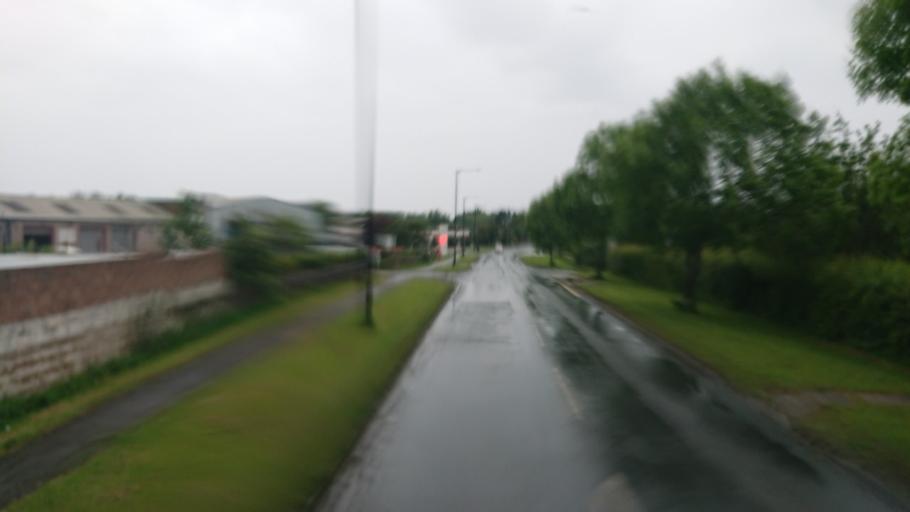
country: GB
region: England
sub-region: Lancashire
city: Morecambe
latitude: 54.0285
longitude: -2.8894
